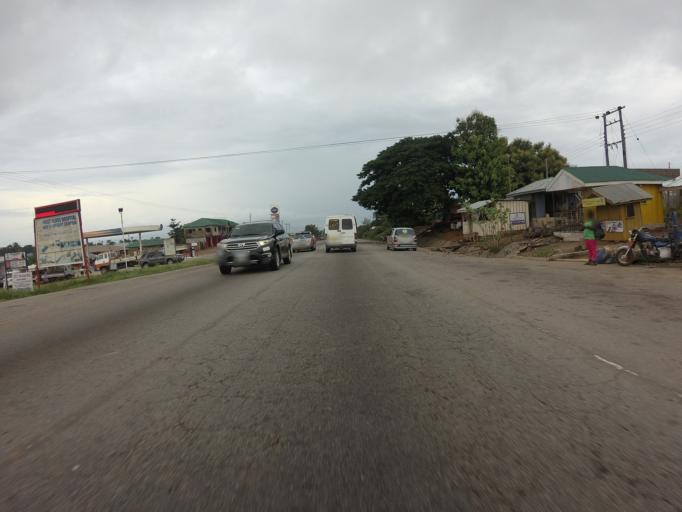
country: GH
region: Ashanti
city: Konongo
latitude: 6.6157
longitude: -1.1577
